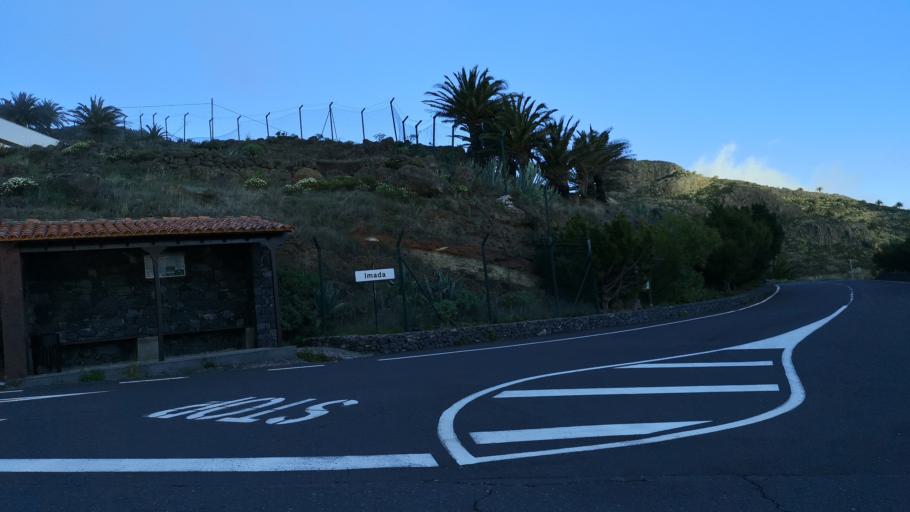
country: ES
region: Canary Islands
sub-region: Provincia de Santa Cruz de Tenerife
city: Alajero
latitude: 28.0761
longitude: -17.2424
